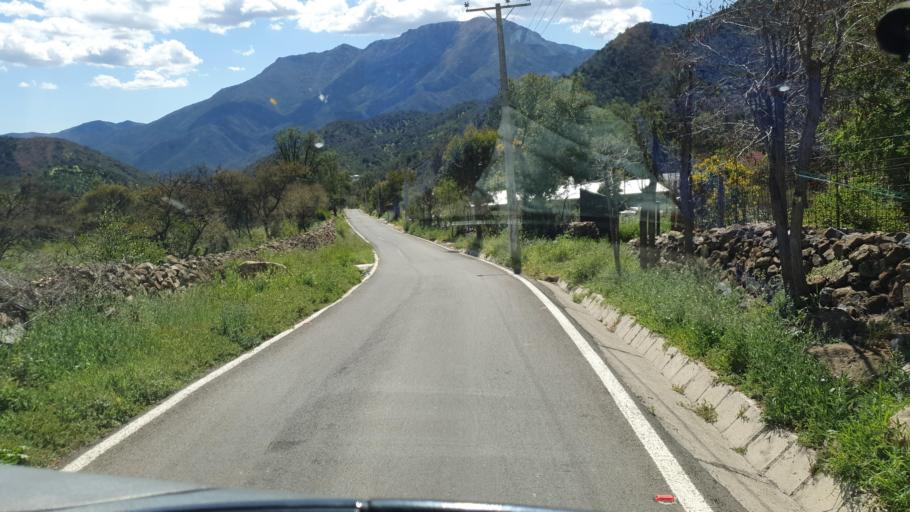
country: CL
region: Santiago Metropolitan
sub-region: Provincia de Chacabuco
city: Lampa
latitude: -33.1922
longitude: -71.0967
